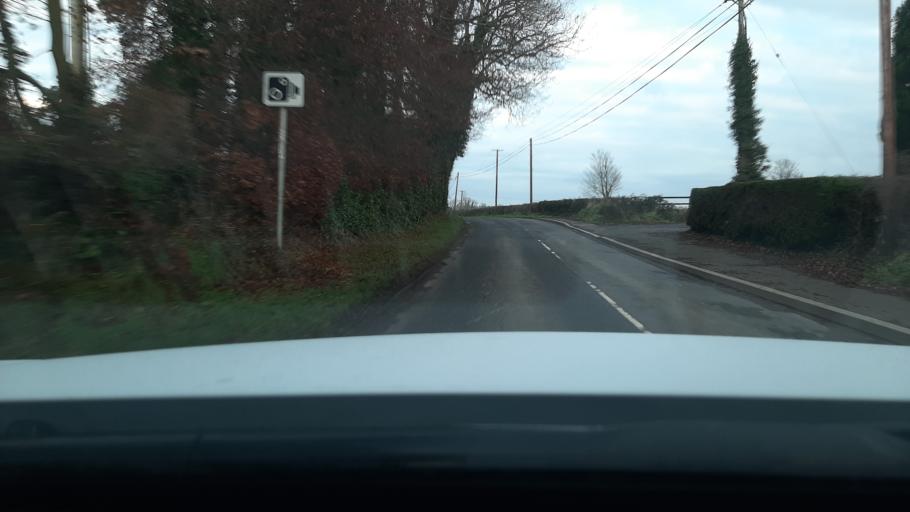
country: IE
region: Leinster
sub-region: Kildare
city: Rathangan
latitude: 53.2264
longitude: -7.0063
